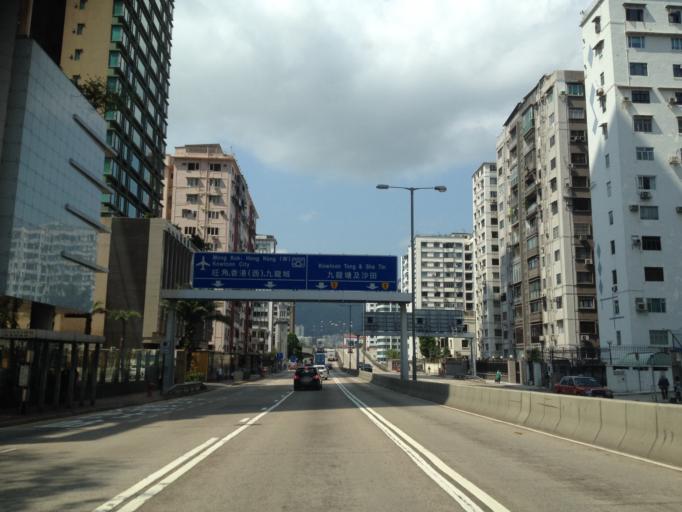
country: HK
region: Kowloon City
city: Kowloon
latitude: 22.3233
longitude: 114.1781
